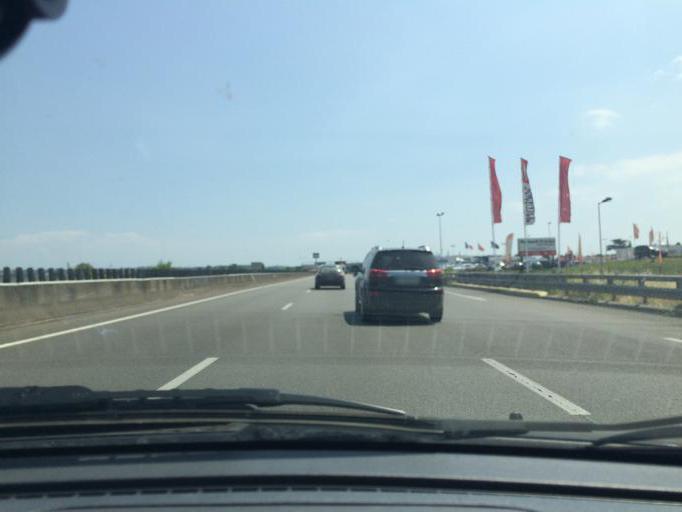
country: FR
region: Rhone-Alpes
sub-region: Departement du Rhone
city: Villefranche-sur-Saone
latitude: 46.0048
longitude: 4.7326
